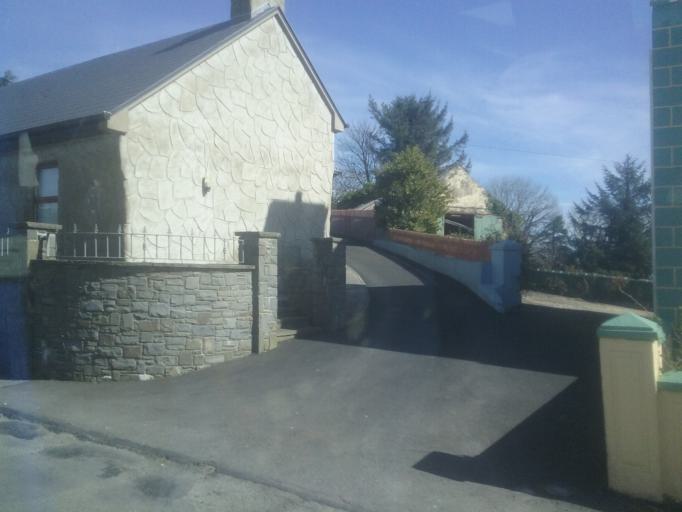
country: IE
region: Munster
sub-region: An Clar
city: Kilrush
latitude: 52.7031
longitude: -9.4181
